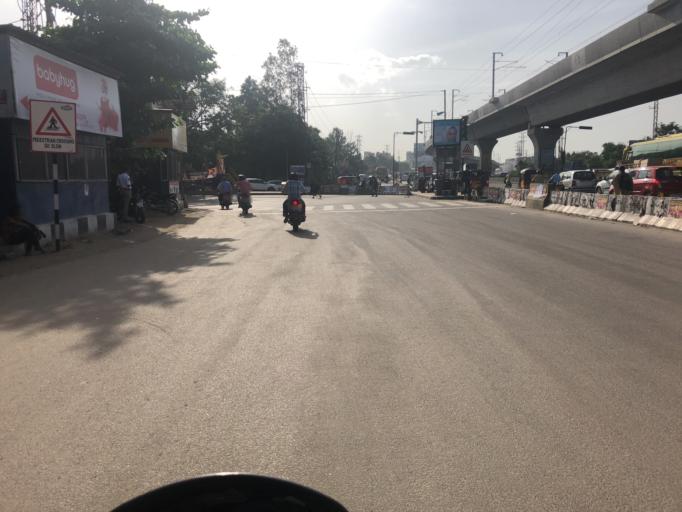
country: IN
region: Telangana
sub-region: Rangareddi
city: Kukatpalli
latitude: 17.4960
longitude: 78.3957
